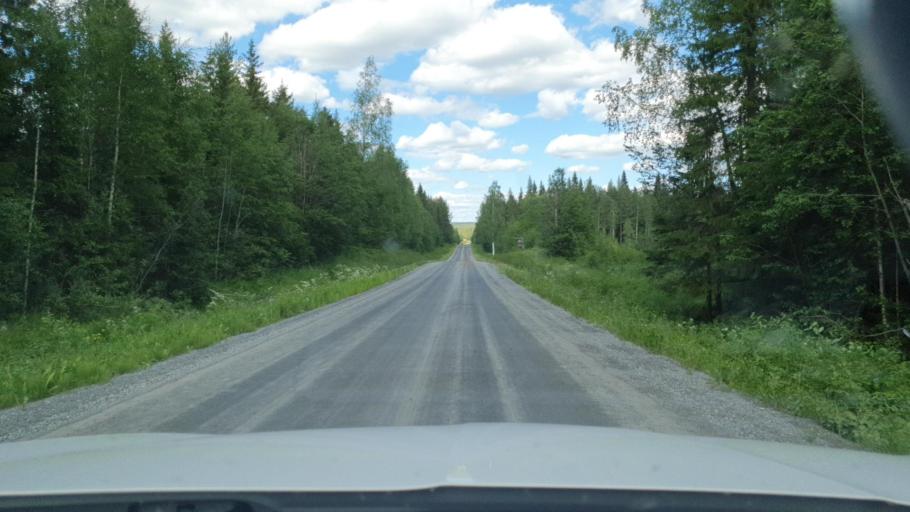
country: SE
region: Vaesterbotten
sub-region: Skelleftea Kommun
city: Forsbacka
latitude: 64.8330
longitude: 20.5020
